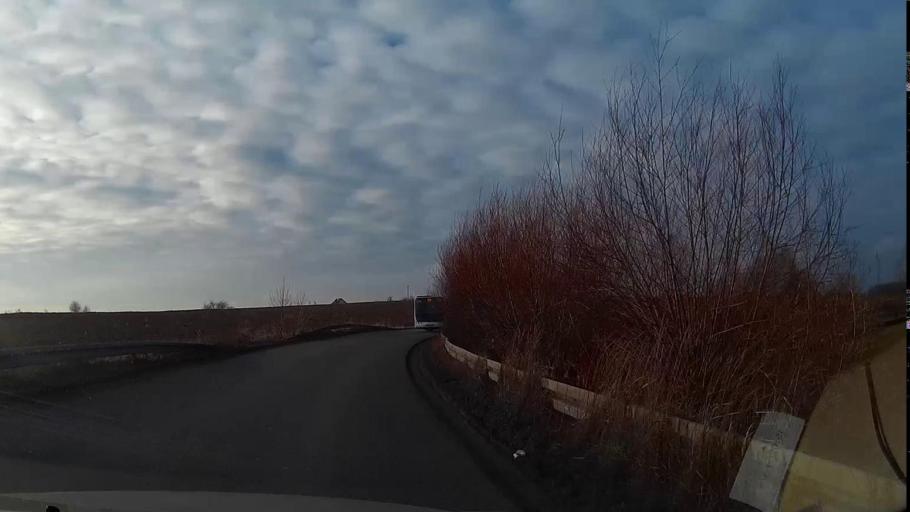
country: PL
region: Lesser Poland Voivodeship
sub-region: Powiat krakowski
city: Sanka
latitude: 50.0620
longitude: 19.6662
